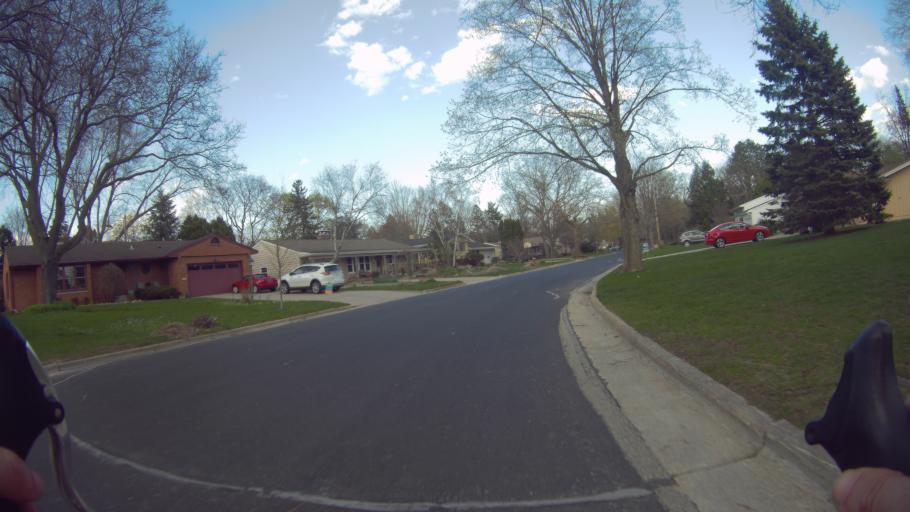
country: US
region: Wisconsin
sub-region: Dane County
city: Shorewood Hills
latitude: 43.0492
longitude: -89.4704
